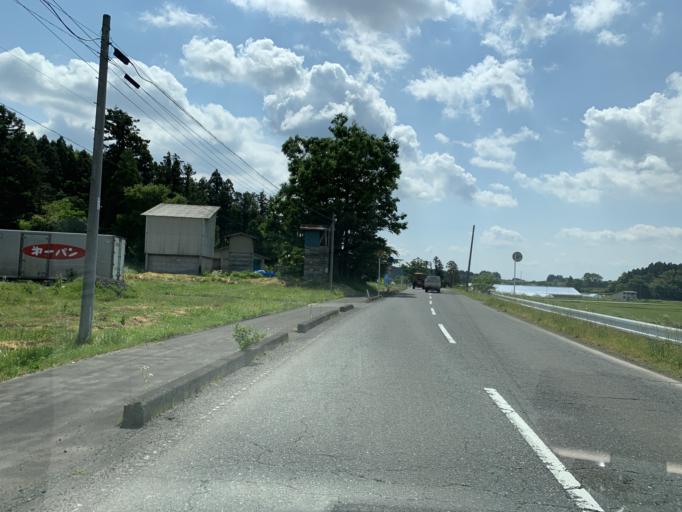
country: JP
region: Miyagi
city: Furukawa
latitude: 38.6874
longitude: 140.9514
